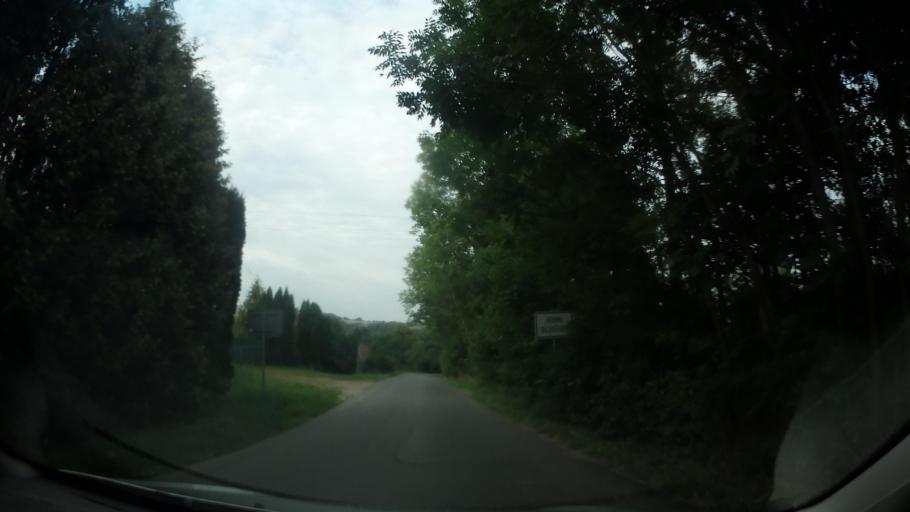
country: CZ
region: Pardubicky
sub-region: Okres Chrudim
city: Sec
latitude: 49.8340
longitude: 15.6961
